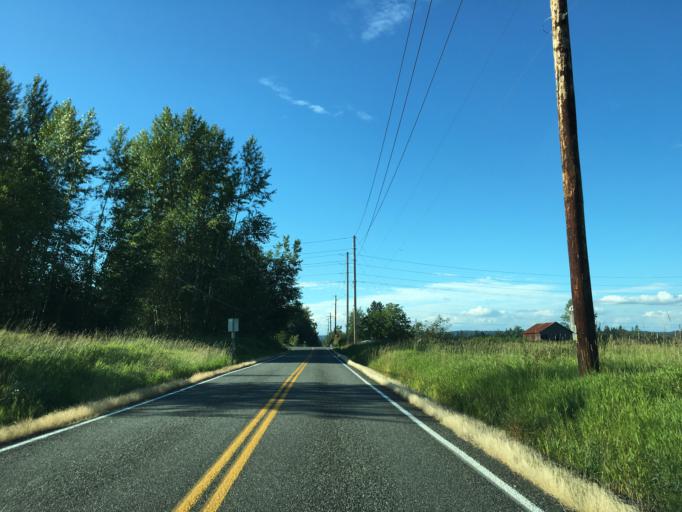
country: US
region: Washington
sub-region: Whatcom County
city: Birch Bay
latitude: 48.9345
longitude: -122.7044
